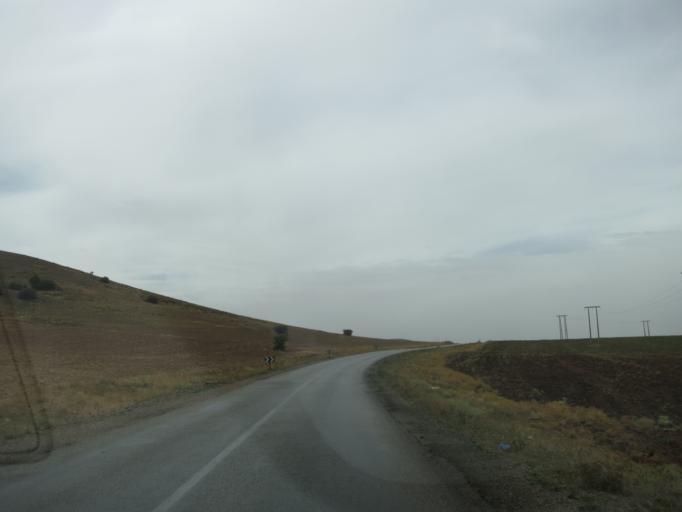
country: MA
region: Meknes-Tafilalet
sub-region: Ifrane
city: Azrou
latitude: 33.1887
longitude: -5.0618
